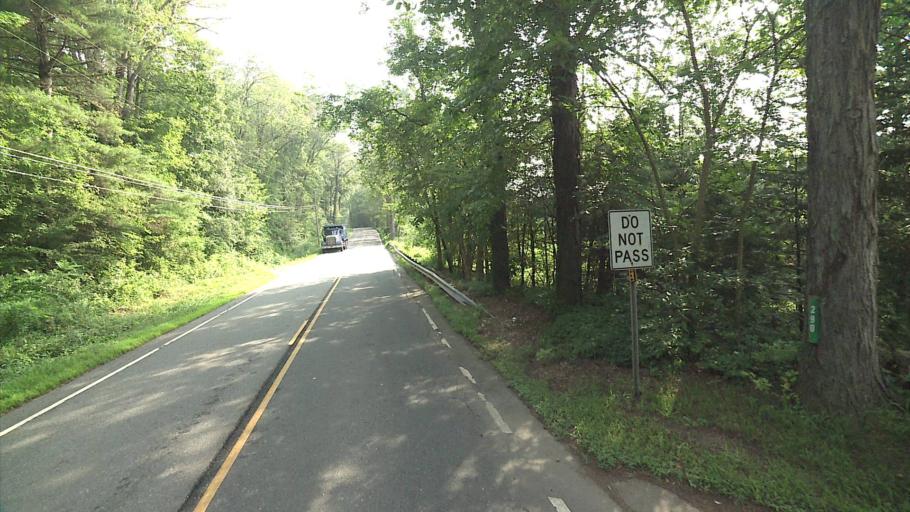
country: US
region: Connecticut
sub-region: Windham County
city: Quinebaug
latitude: 42.0033
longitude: -71.9760
